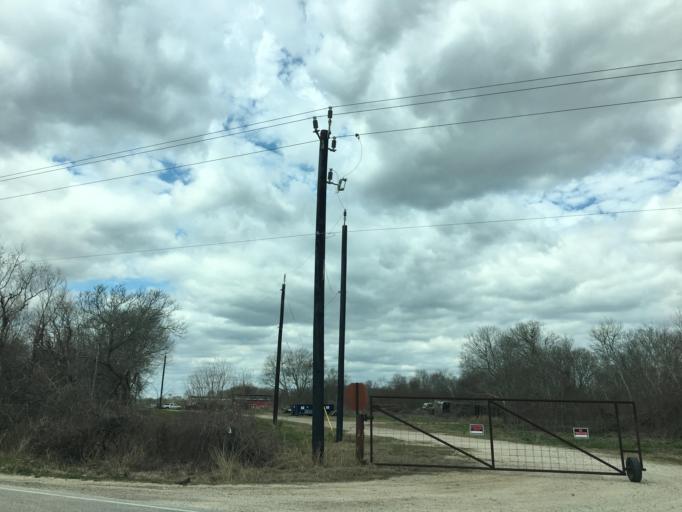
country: US
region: Texas
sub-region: Brazoria County
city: Oyster Creek
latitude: 29.0652
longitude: -95.3193
